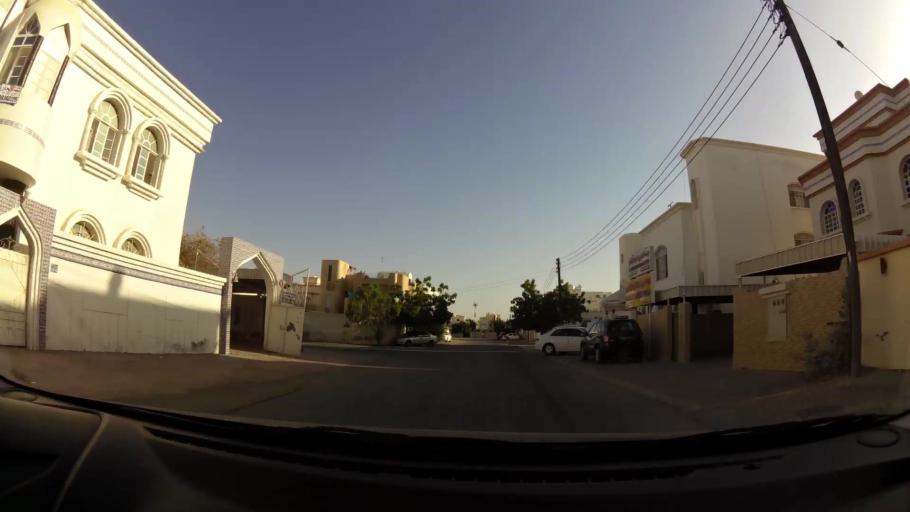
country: OM
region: Muhafazat Masqat
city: As Sib al Jadidah
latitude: 23.6351
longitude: 58.1973
